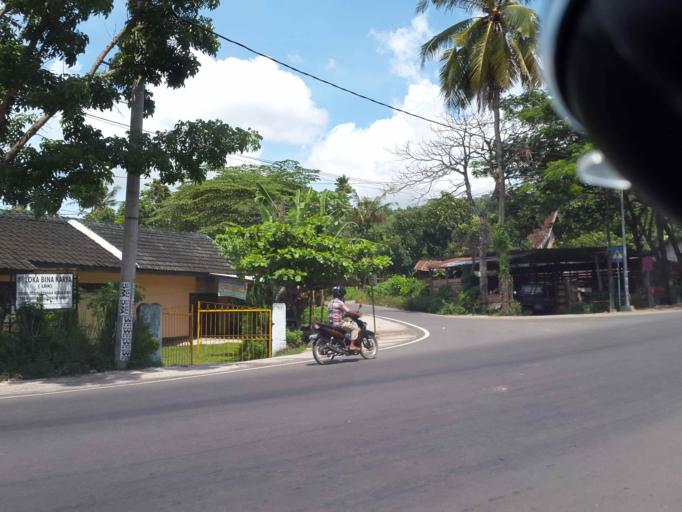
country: ID
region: West Nusa Tenggara
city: Kediri
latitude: -8.6889
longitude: 116.1161
